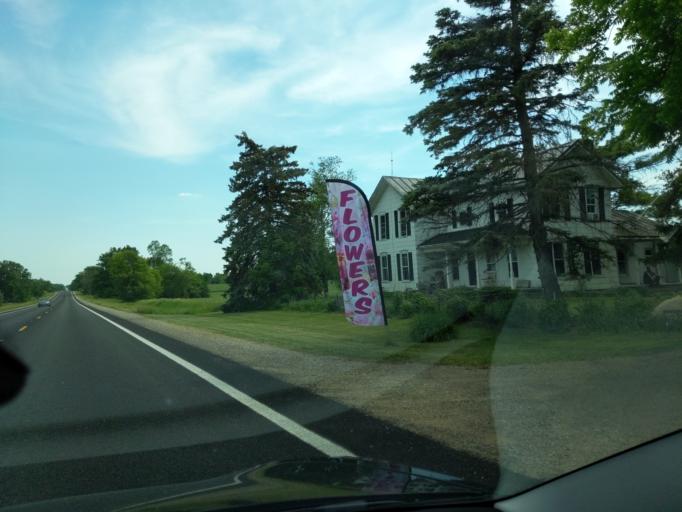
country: US
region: Michigan
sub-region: Ionia County
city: Lake Odessa
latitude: 42.7077
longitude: -85.0952
